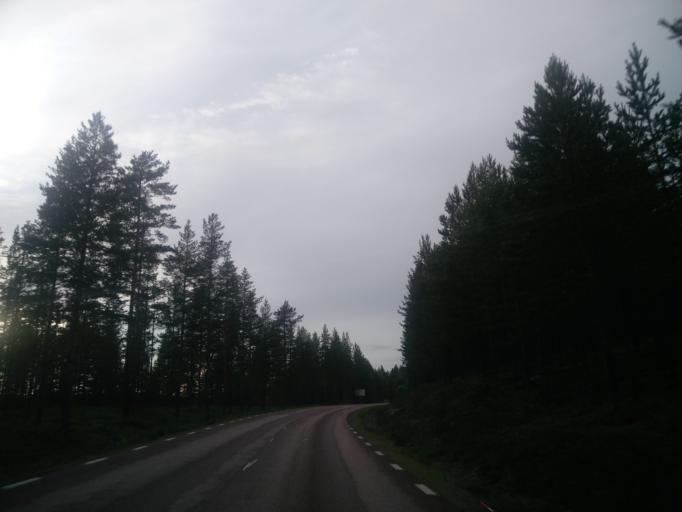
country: NO
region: Hedmark
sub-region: Trysil
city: Innbygda
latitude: 61.7916
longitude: 12.9253
